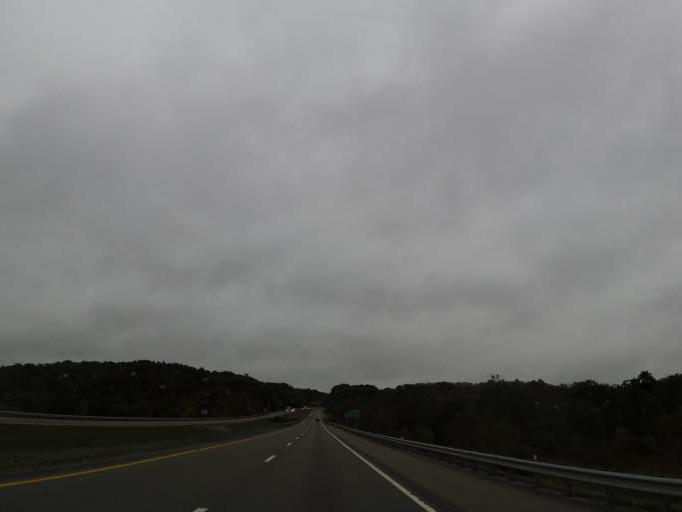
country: US
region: Virginia
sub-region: Wythe County
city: Wytheville
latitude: 36.9842
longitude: -81.0735
